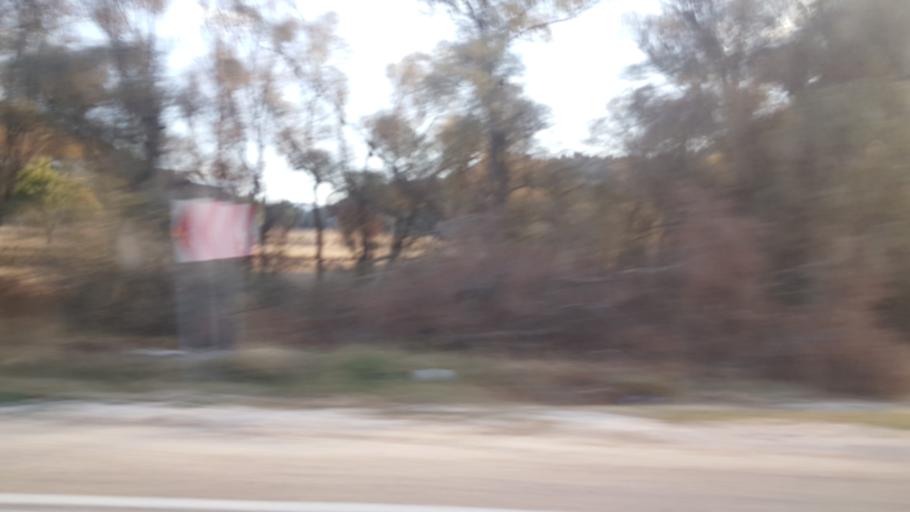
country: TR
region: Eskisehir
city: Kirka
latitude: 39.3571
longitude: 30.5924
